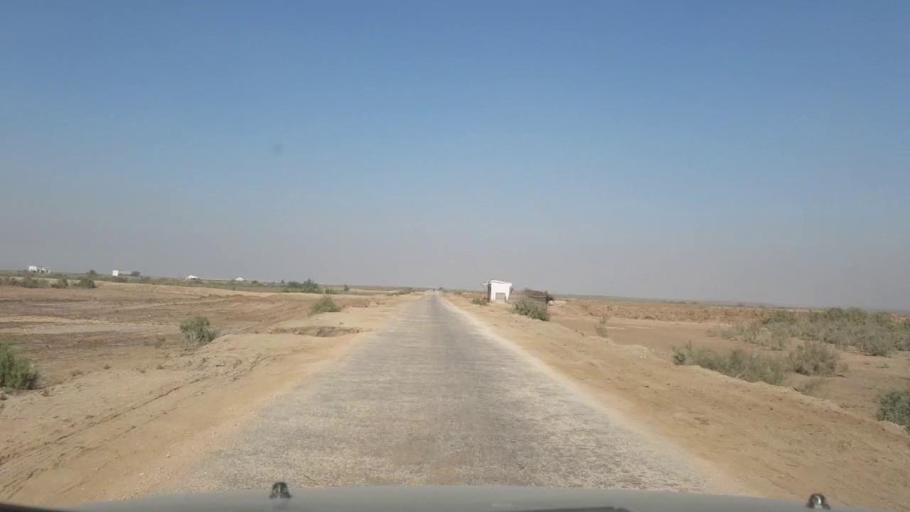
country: PK
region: Sindh
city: Thatta
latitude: 24.8140
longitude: 67.8975
